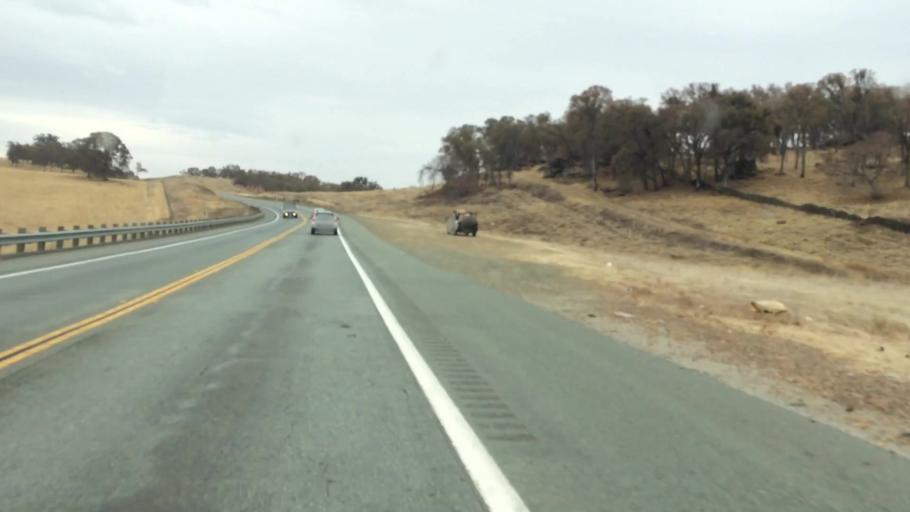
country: US
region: California
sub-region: Amador County
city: Sutter Creek
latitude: 38.3937
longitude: -120.8163
